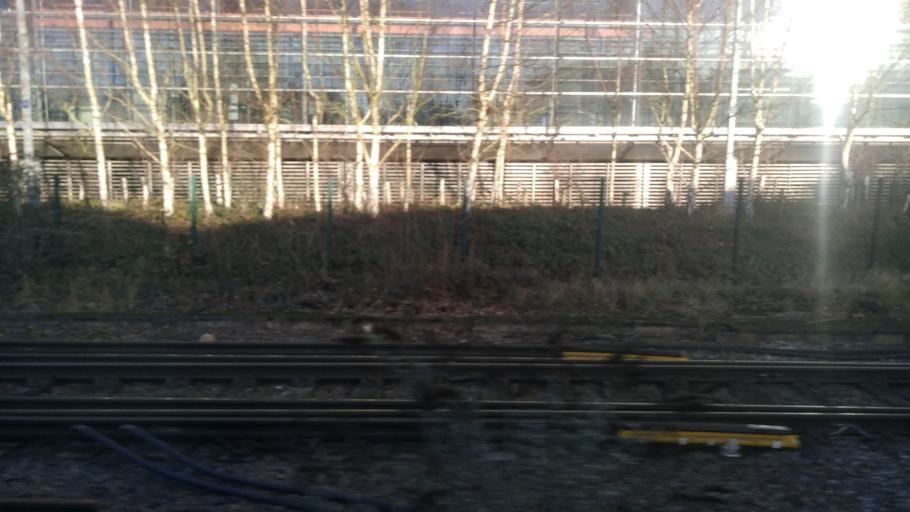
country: GB
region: England
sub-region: Kent
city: Sevenoaks
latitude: 51.2780
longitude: 0.1811
